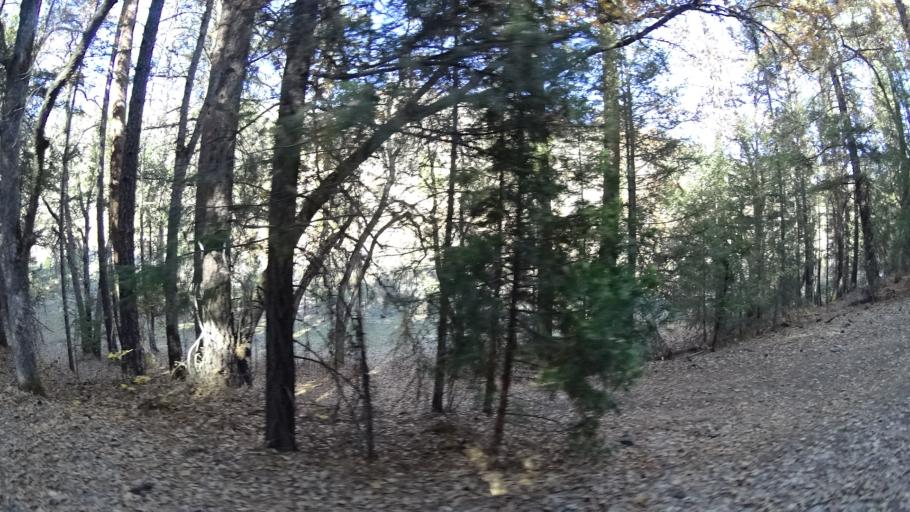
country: US
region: California
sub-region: Siskiyou County
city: Yreka
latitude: 41.8572
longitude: -122.7519
